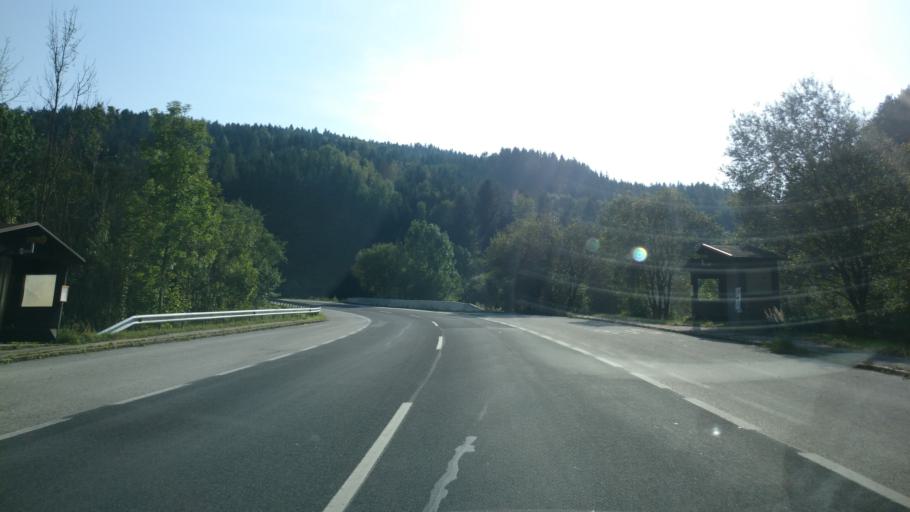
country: AT
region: Lower Austria
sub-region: Politischer Bezirk Neunkirchen
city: Zobern
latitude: 47.5439
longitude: 16.0752
